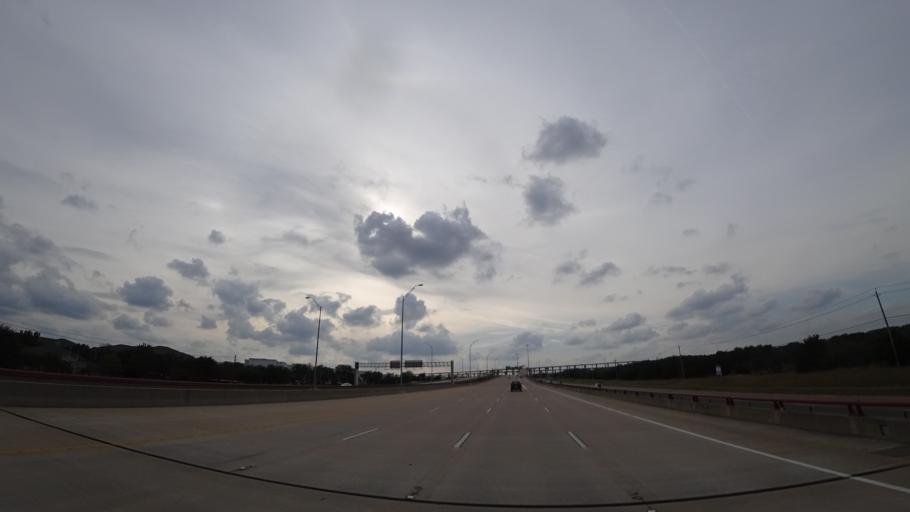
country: US
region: Texas
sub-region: Williamson County
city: Anderson Mill
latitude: 30.4725
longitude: -97.7847
